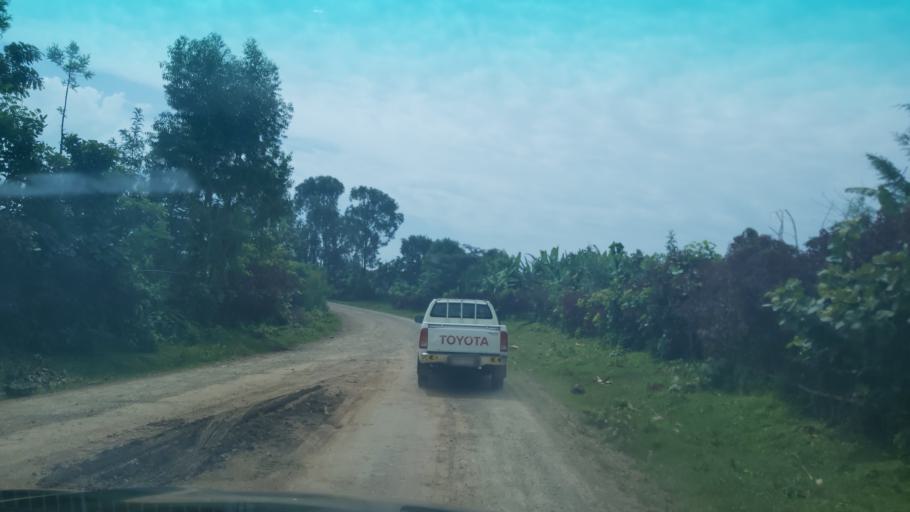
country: ET
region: Oromiya
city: Jima
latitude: 7.7407
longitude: 36.7872
